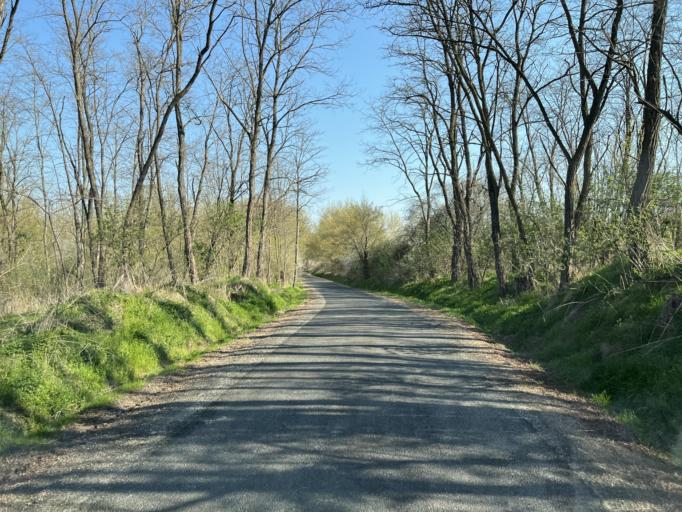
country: SK
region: Nitriansky
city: Sahy
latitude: 48.0242
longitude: 18.8275
